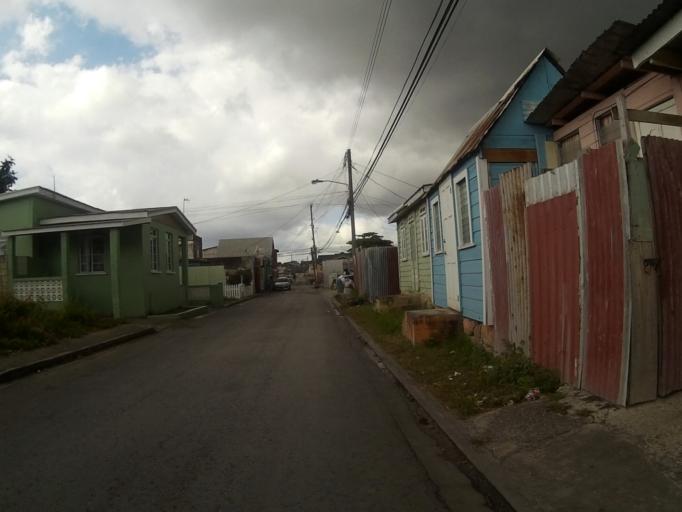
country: BB
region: Saint Michael
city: Bridgetown
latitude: 13.1021
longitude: -59.6039
